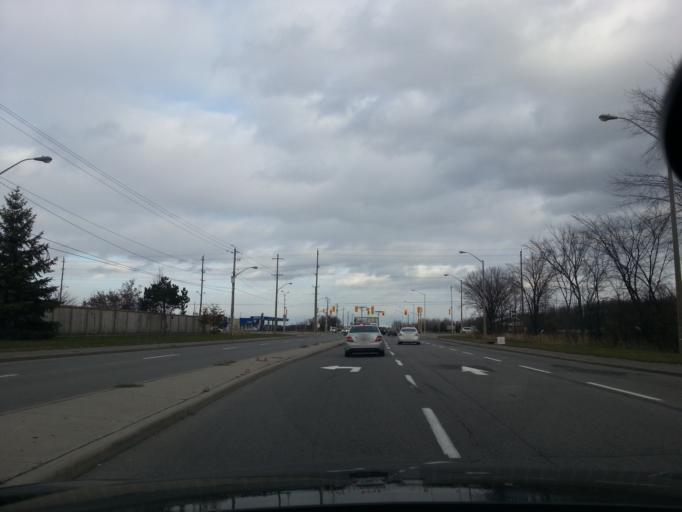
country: CA
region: Ontario
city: Ottawa
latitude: 45.3734
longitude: -75.5988
